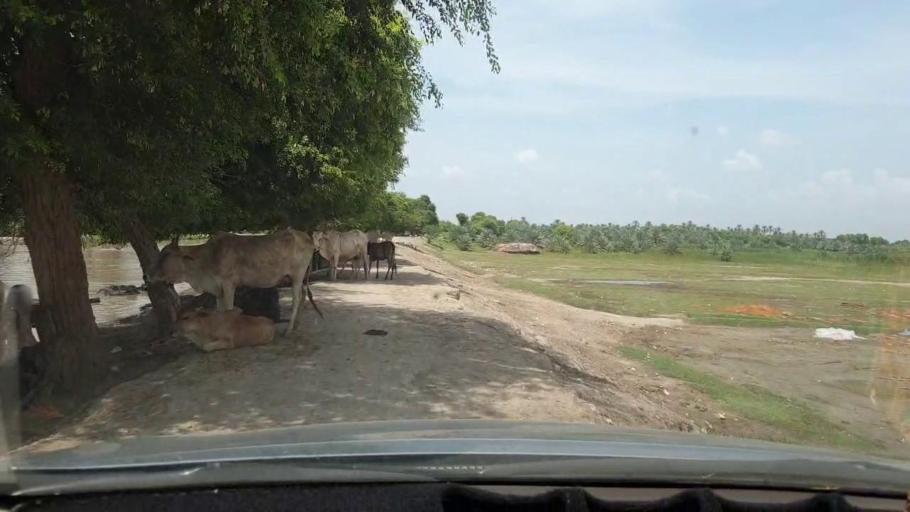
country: PK
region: Sindh
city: Khairpur
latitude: 27.4449
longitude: 68.7962
